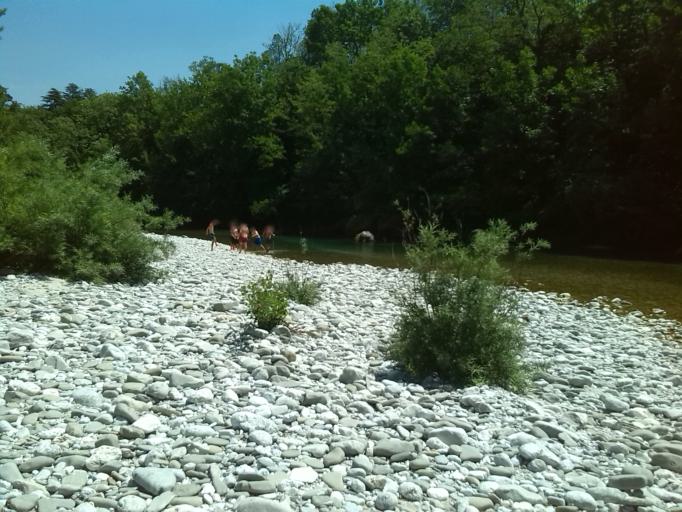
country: IT
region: Friuli Venezia Giulia
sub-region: Provincia di Udine
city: Cividale del Friuli
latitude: 46.0935
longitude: 13.4402
